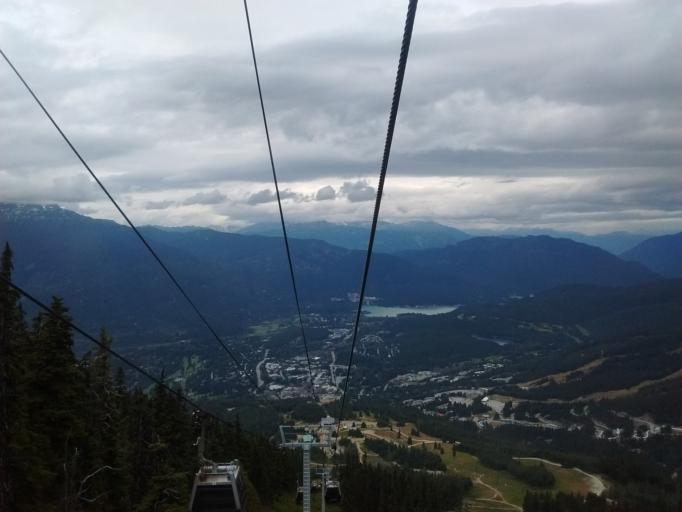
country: CA
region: British Columbia
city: Whistler
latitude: 50.0853
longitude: -122.9498
